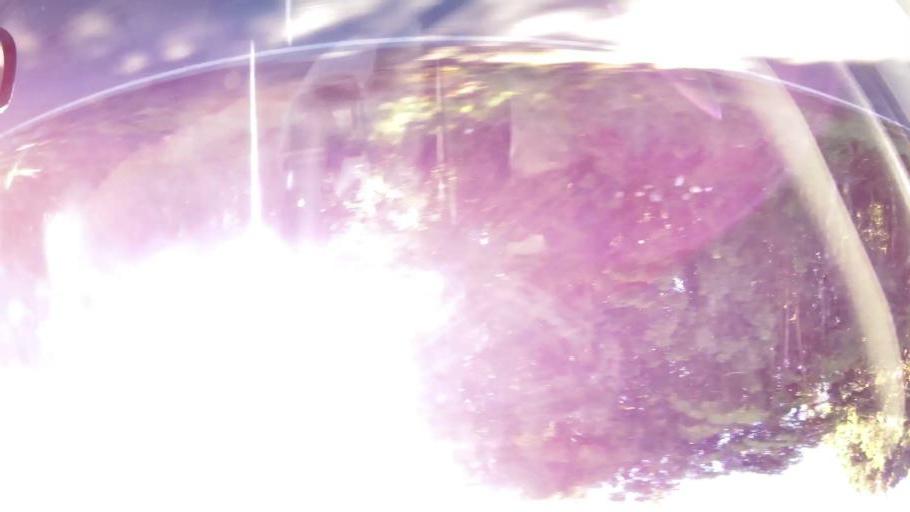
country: CR
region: San Jose
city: San Marcos
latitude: 9.6873
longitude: -83.9213
